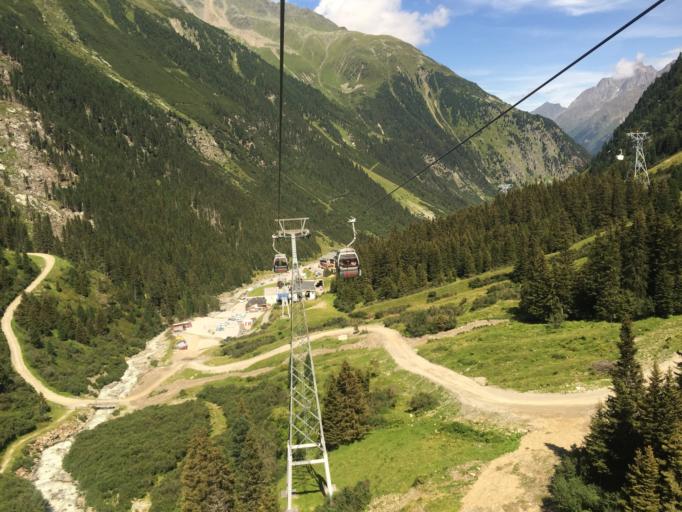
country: AT
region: Tyrol
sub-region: Politischer Bezirk Imst
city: Soelden
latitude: 47.0073
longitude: 11.1515
